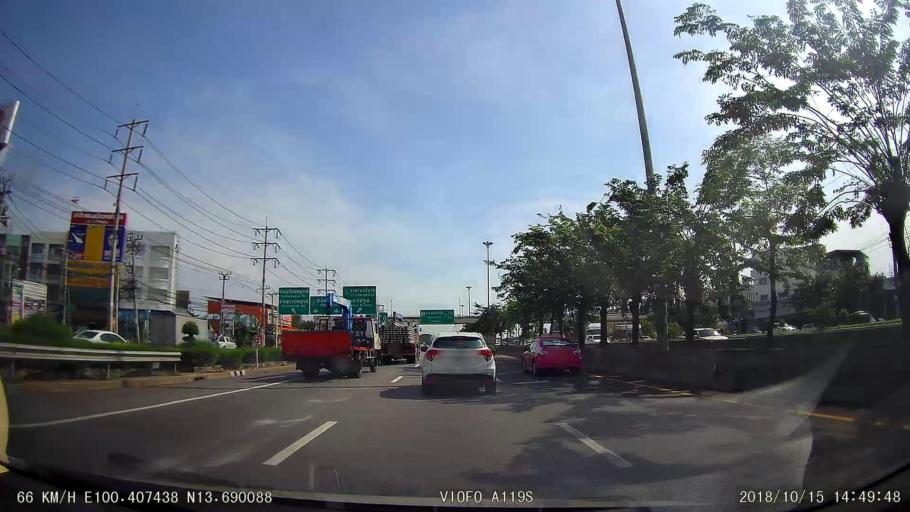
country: TH
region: Bangkok
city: Bang Khae
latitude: 13.6900
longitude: 100.4074
